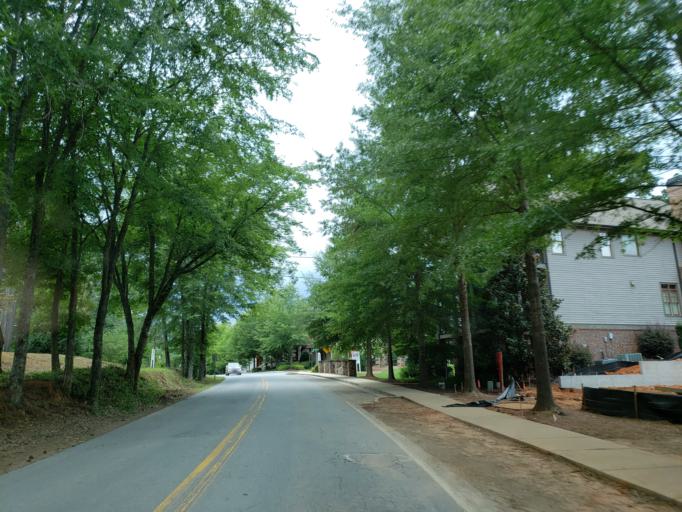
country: US
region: Georgia
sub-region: Cherokee County
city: Woodstock
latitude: 34.1107
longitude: -84.5252
